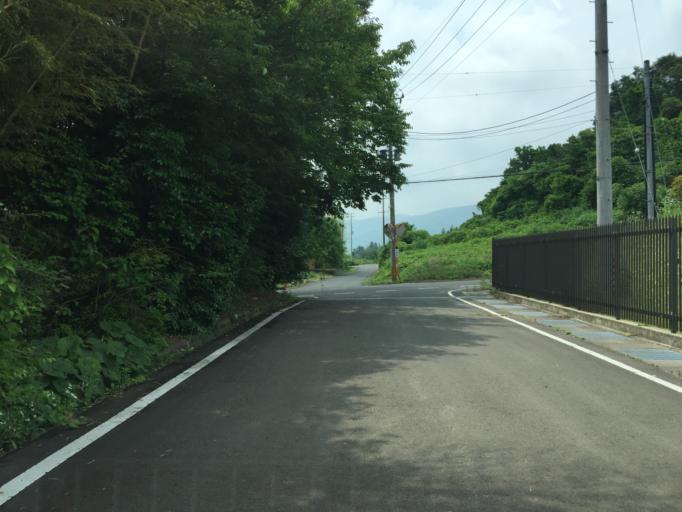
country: JP
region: Fukushima
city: Fukushima-shi
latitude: 37.7723
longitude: 140.3746
